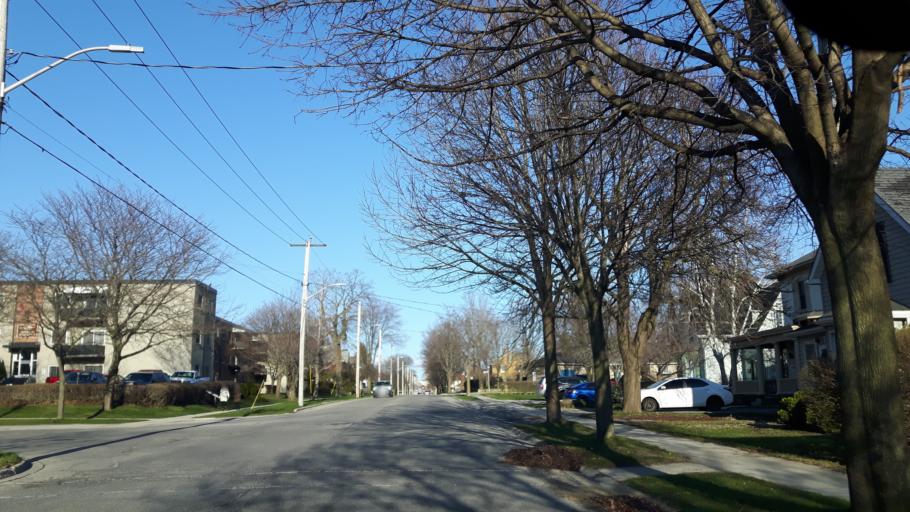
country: CA
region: Ontario
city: Goderich
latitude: 43.7392
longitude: -81.7149
